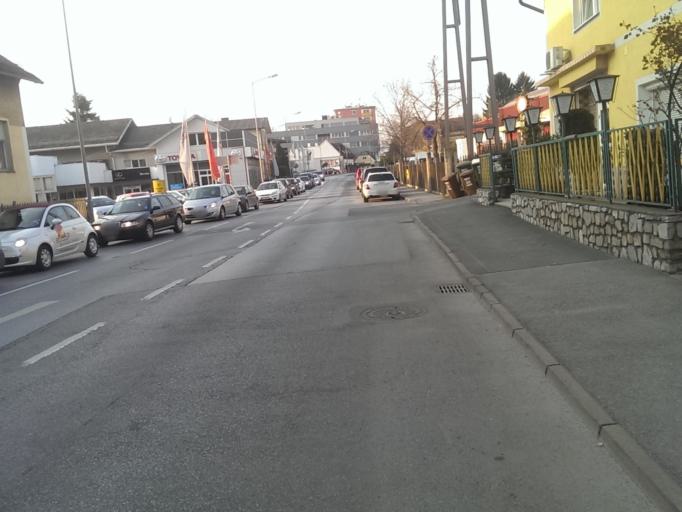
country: AT
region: Styria
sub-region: Graz Stadt
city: Graz
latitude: 47.0425
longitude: 15.4586
